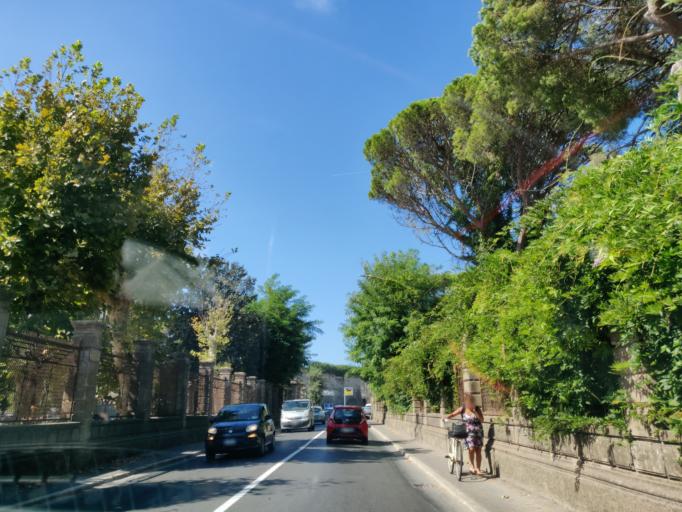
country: IT
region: Tuscany
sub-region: Provincia di Grosseto
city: Orbetello
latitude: 42.4412
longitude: 11.2161
